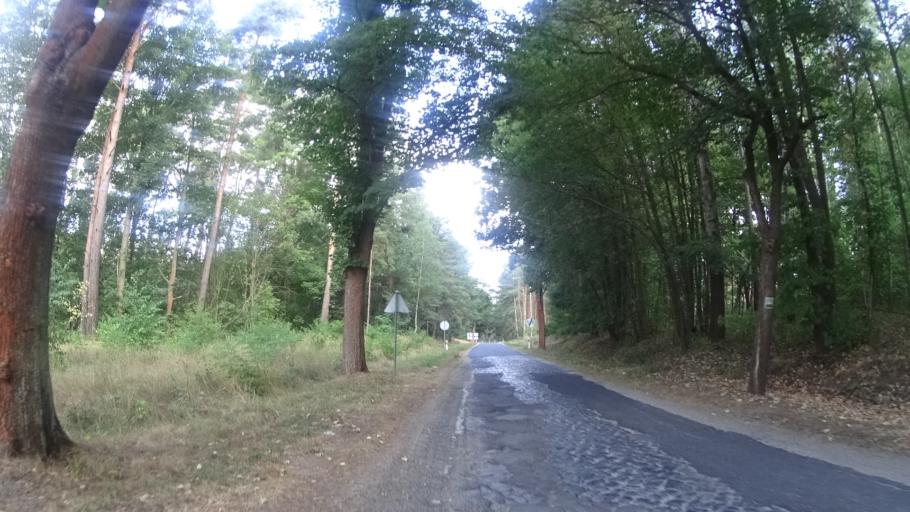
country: PL
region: Lubusz
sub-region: Powiat zarski
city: Przewoz
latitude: 51.4956
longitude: 14.8578
